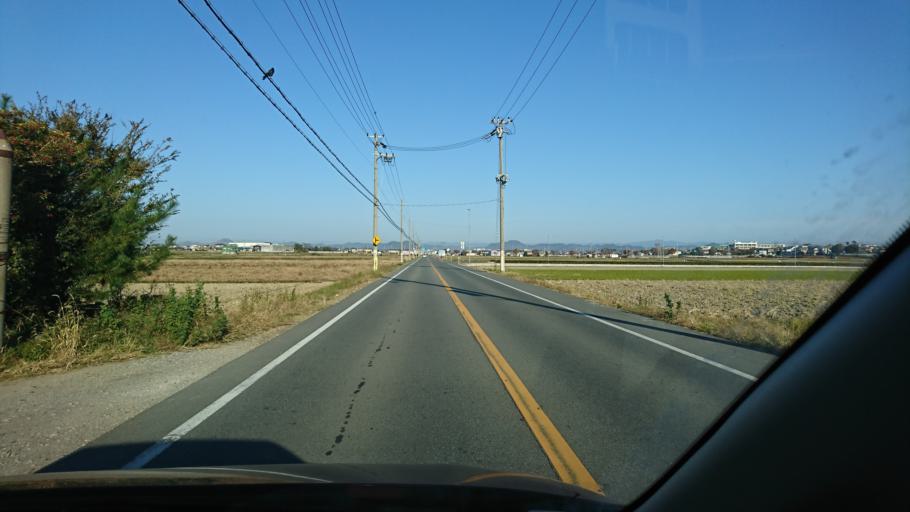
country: JP
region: Hyogo
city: Kakogawacho-honmachi
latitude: 34.7396
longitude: 134.9033
